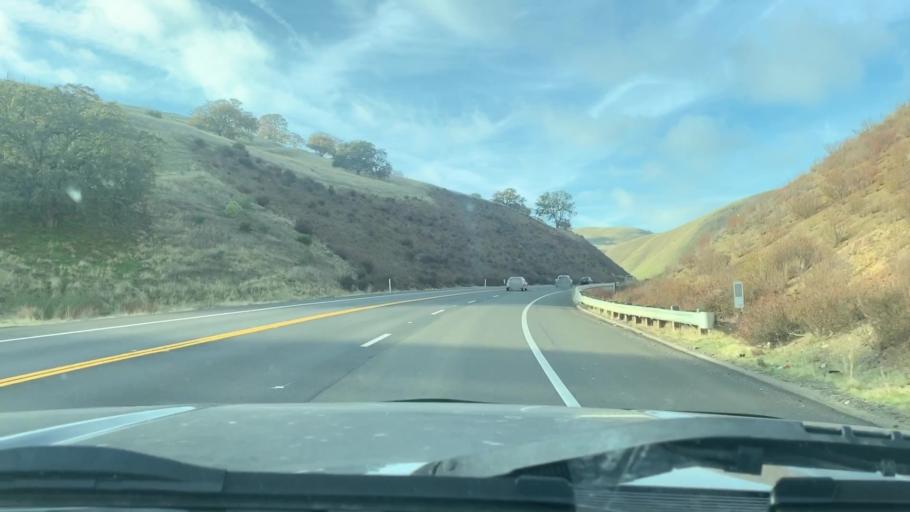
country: US
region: California
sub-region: San Luis Obispo County
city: Shandon
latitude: 35.7742
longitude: -120.1801
